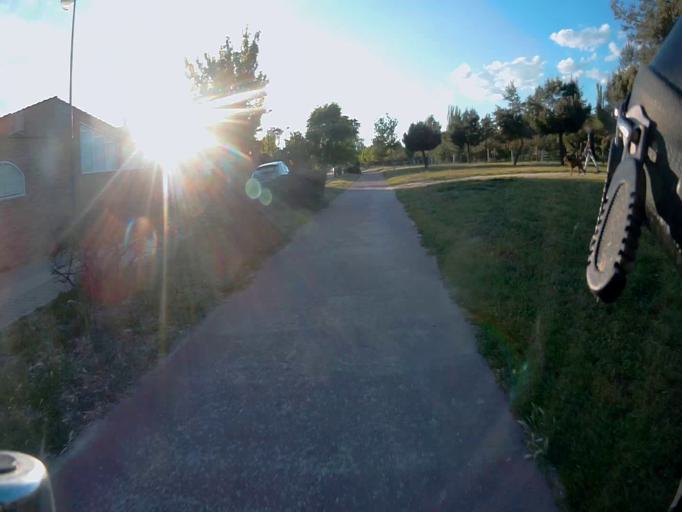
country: ES
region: Madrid
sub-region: Provincia de Madrid
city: Fuenlabrada
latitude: 40.3119
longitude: -3.7900
